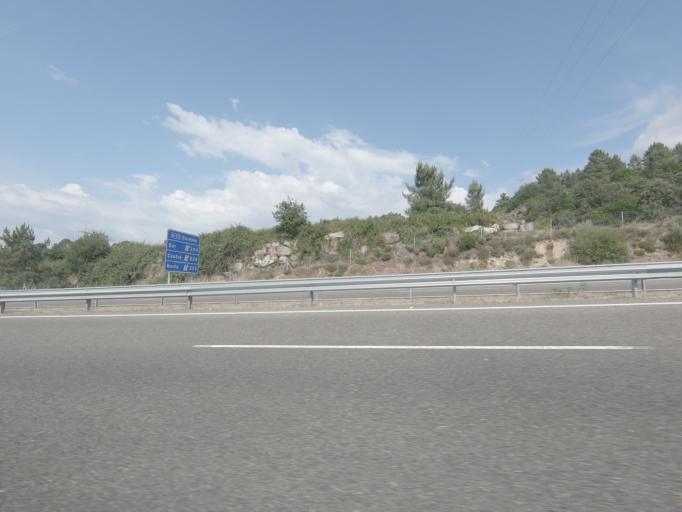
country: ES
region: Galicia
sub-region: Provincia de Ourense
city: Ourense
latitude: 42.2793
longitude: -7.8725
